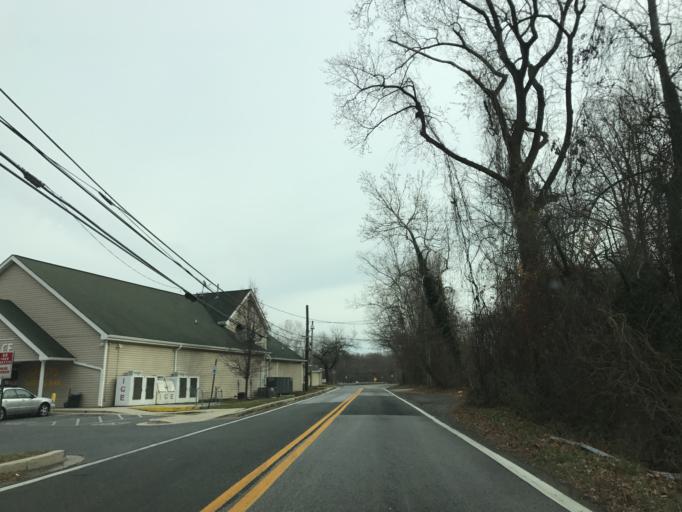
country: US
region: Maryland
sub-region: Anne Arundel County
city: Severna Park
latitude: 39.0552
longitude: -76.5267
